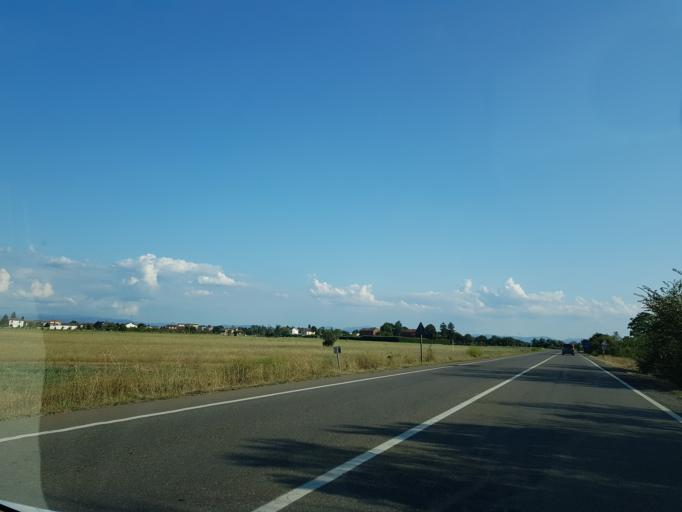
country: IT
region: Piedmont
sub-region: Provincia di Alessandria
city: Litta Parodi-Cascinagrossa
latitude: 44.8743
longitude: 8.6975
